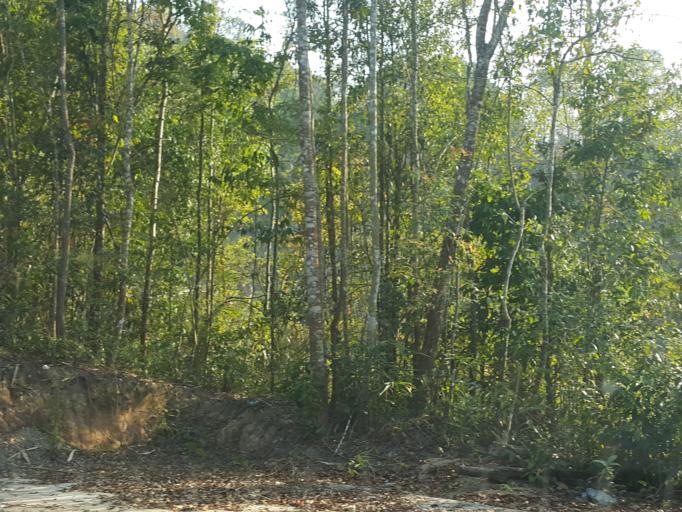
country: TH
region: Chiang Mai
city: Samoeng
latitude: 19.0159
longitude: 98.7621
